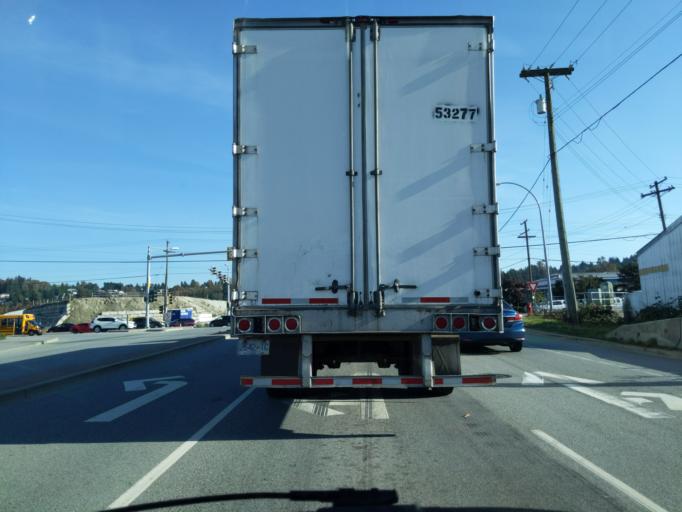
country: CA
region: British Columbia
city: New Westminster
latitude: 49.1942
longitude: -122.8895
